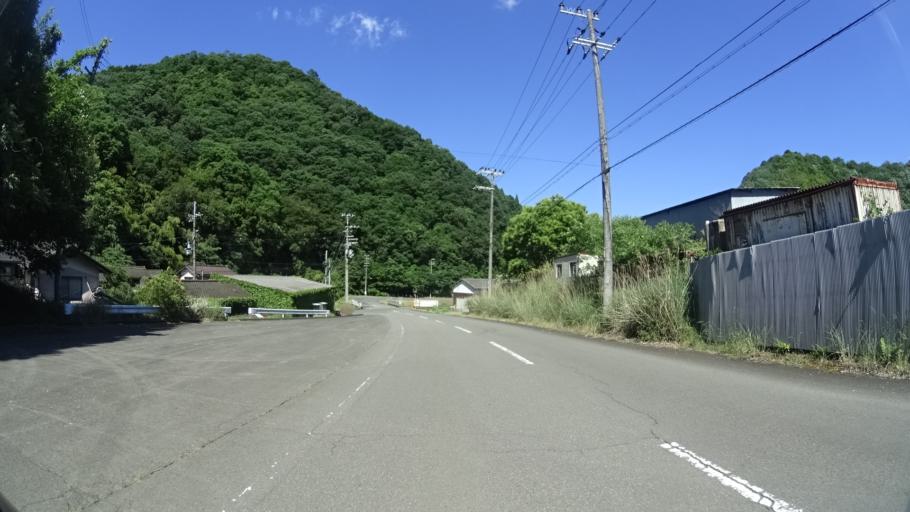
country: JP
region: Kyoto
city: Fukuchiyama
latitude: 35.3606
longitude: 135.1031
